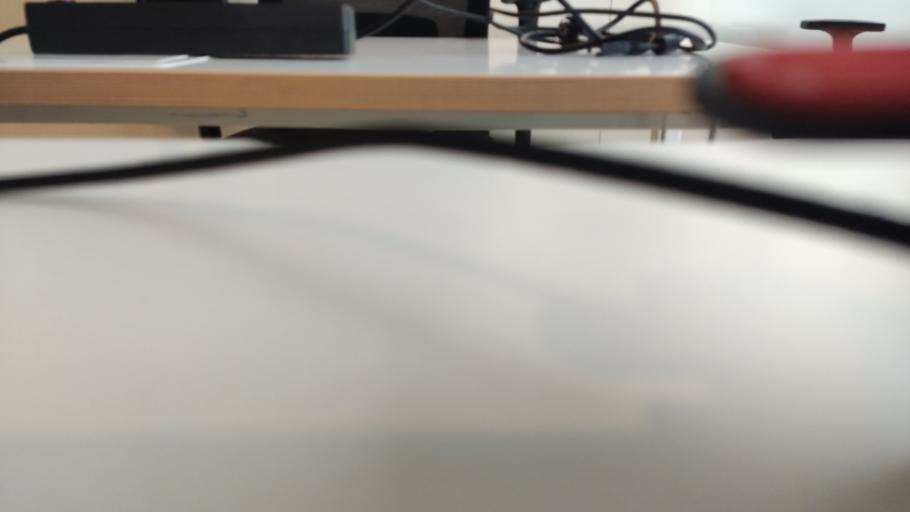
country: RU
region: Moskovskaya
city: Shevlyakovo
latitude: 56.4176
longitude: 36.9460
